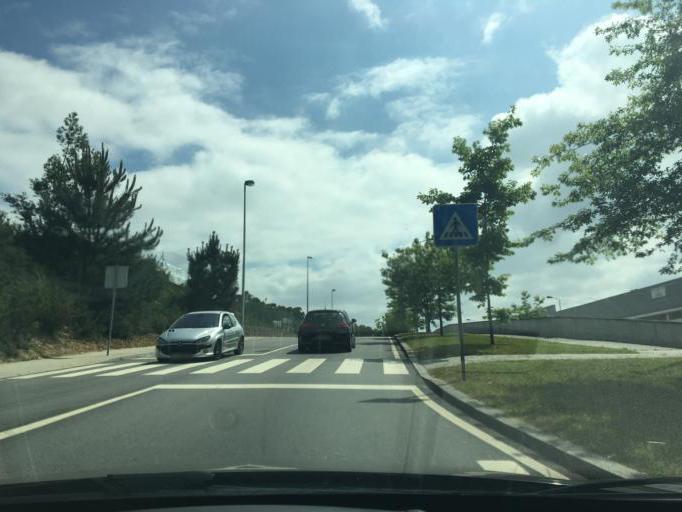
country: PT
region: Porto
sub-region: Maia
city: Gemunde
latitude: 41.2544
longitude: -8.6412
